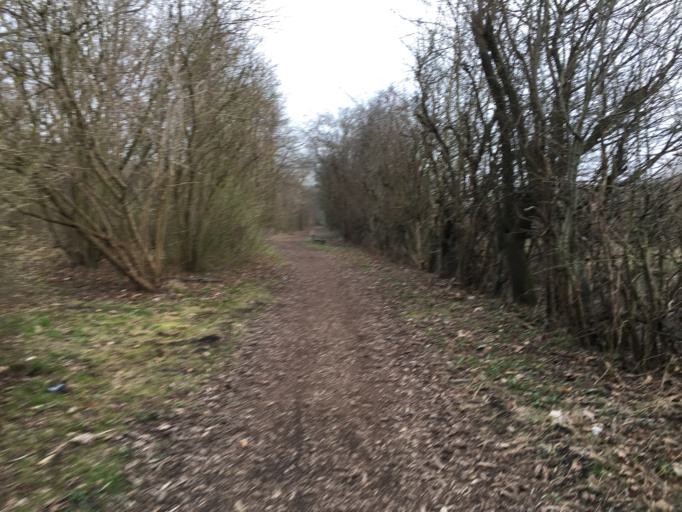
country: SE
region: Skane
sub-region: Lomma Kommun
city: Lomma
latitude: 55.6566
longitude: 13.0750
